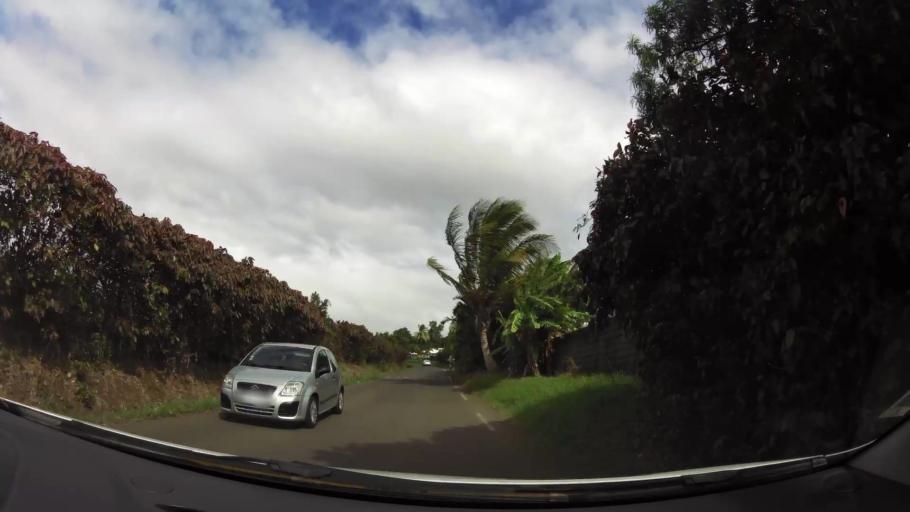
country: RE
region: Reunion
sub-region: Reunion
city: Sainte-Marie
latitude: -20.9001
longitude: 55.5699
